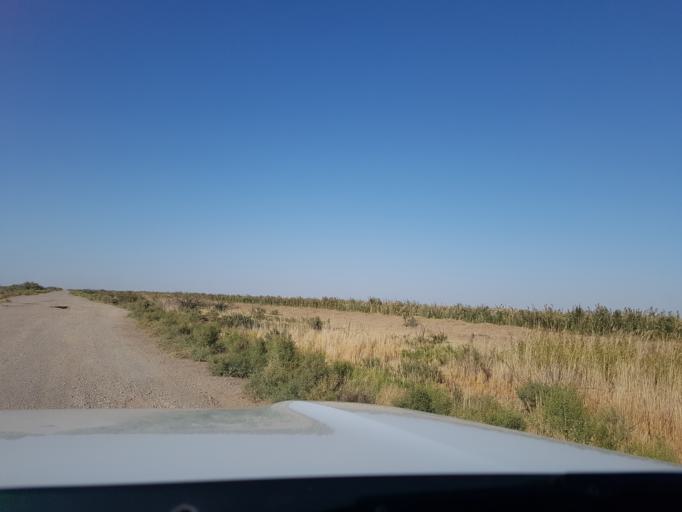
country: IR
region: Razavi Khorasan
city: Sarakhs
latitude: 36.9474
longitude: 61.3792
